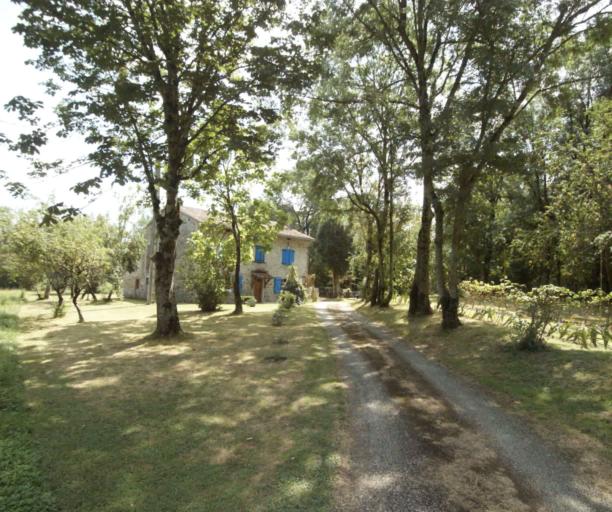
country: FR
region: Midi-Pyrenees
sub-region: Departement du Tarn
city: Soreze
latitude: 43.4743
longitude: 2.0778
